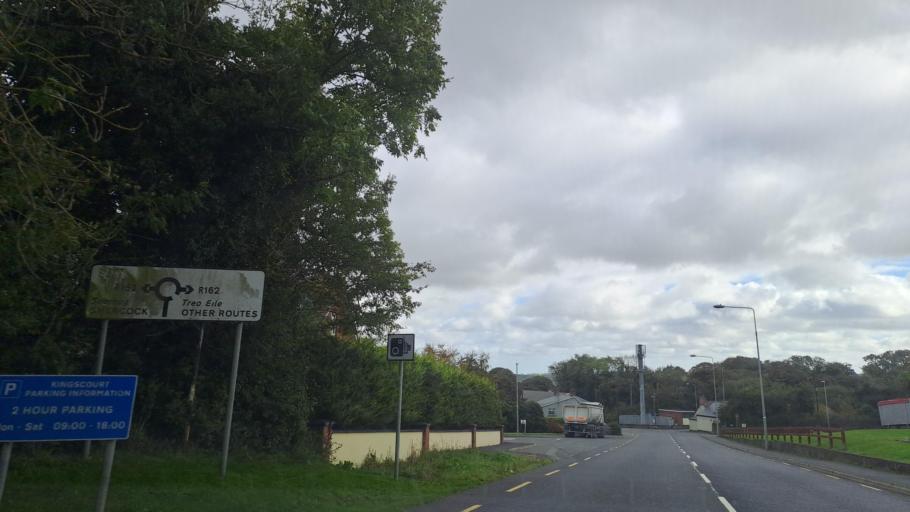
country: IE
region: Ulster
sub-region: An Cabhan
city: Kingscourt
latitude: 53.9084
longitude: -6.8101
